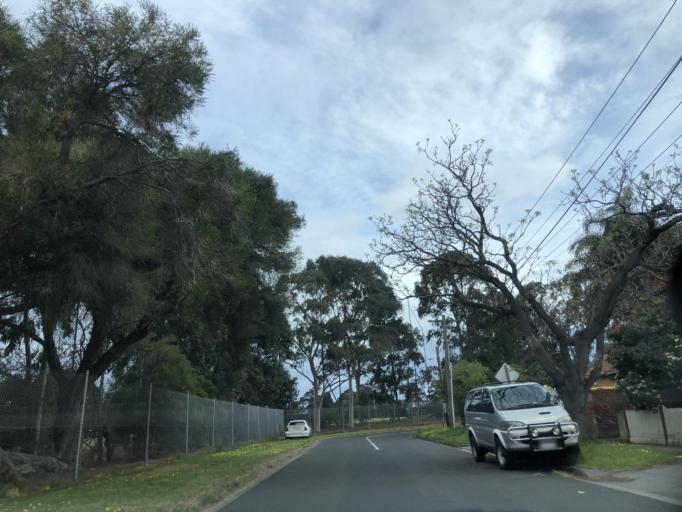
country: AU
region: Victoria
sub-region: Monash
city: Oakleigh South
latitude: -37.9272
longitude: 145.0858
